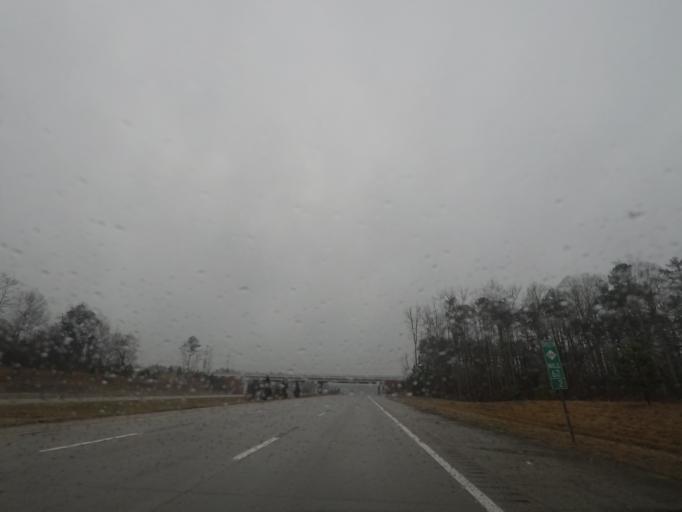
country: US
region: North Carolina
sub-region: Wake County
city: Green Level
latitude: 35.7848
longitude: -78.8870
